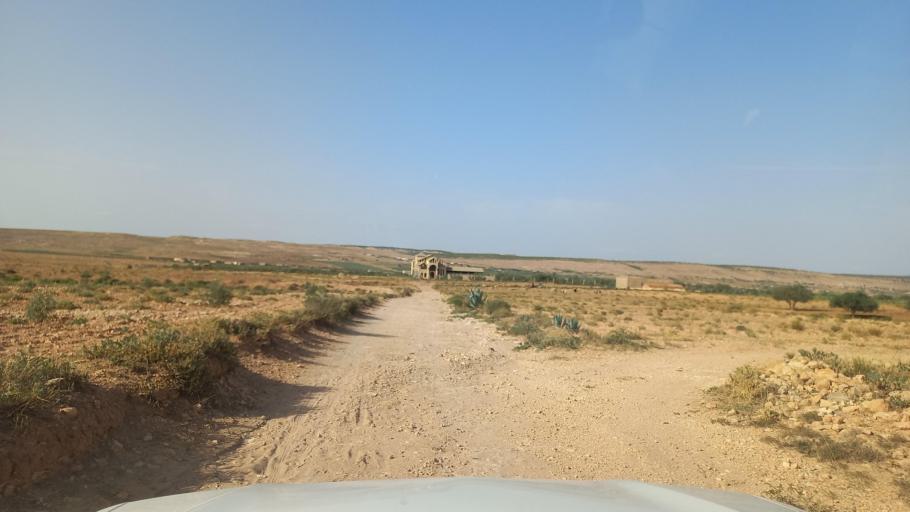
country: TN
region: Al Qasrayn
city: Kasserine
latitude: 35.3407
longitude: 8.8453
